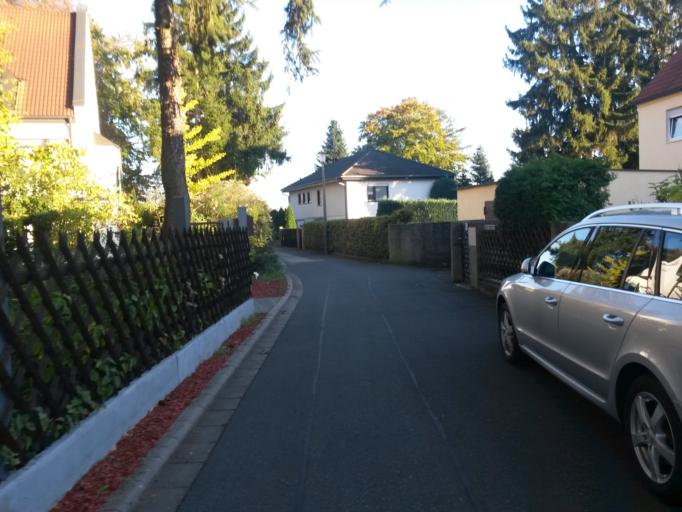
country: DE
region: Bavaria
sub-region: Regierungsbezirk Mittelfranken
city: Zirndorf
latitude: 49.4491
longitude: 10.9708
